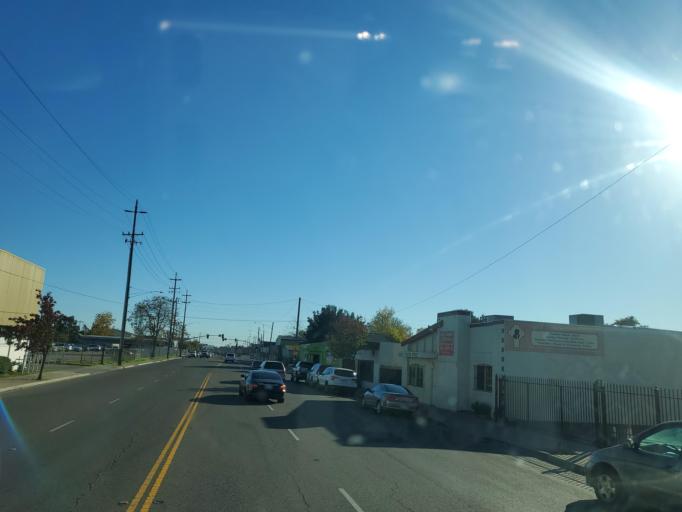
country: US
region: California
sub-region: San Joaquin County
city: Stockton
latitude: 37.9515
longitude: -121.2703
